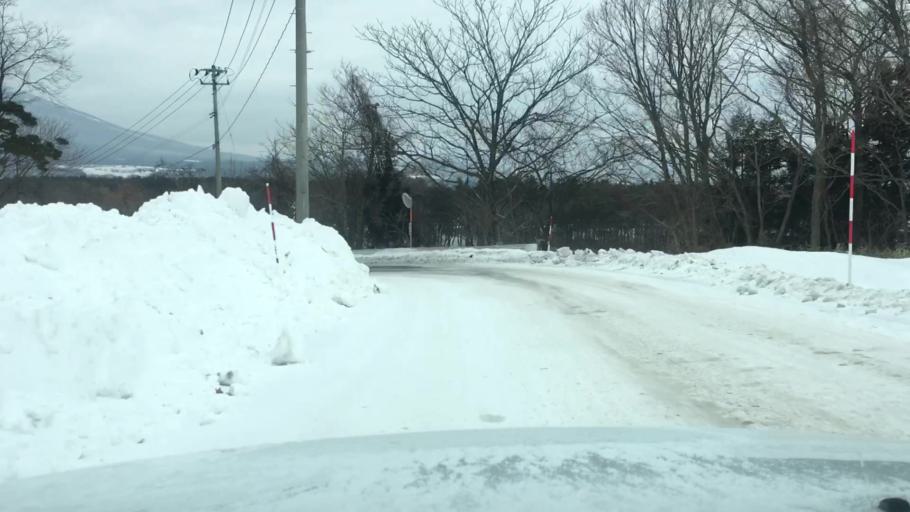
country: JP
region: Iwate
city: Shizukuishi
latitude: 39.9108
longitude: 141.0055
